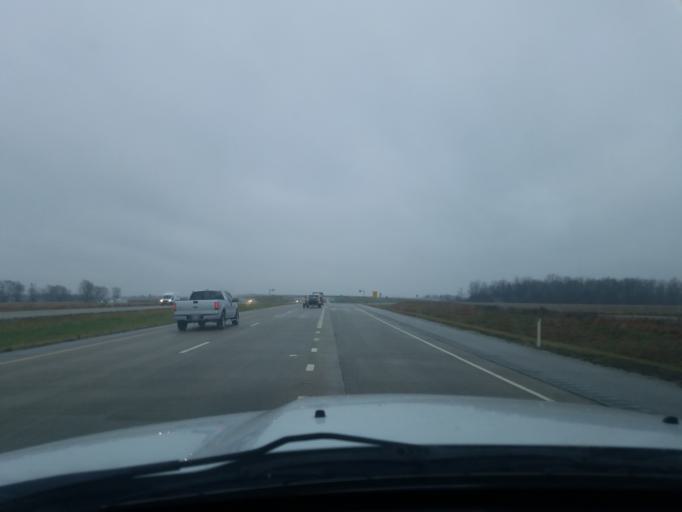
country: US
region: Indiana
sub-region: Howard County
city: Indian Heights
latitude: 40.4246
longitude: -86.0878
